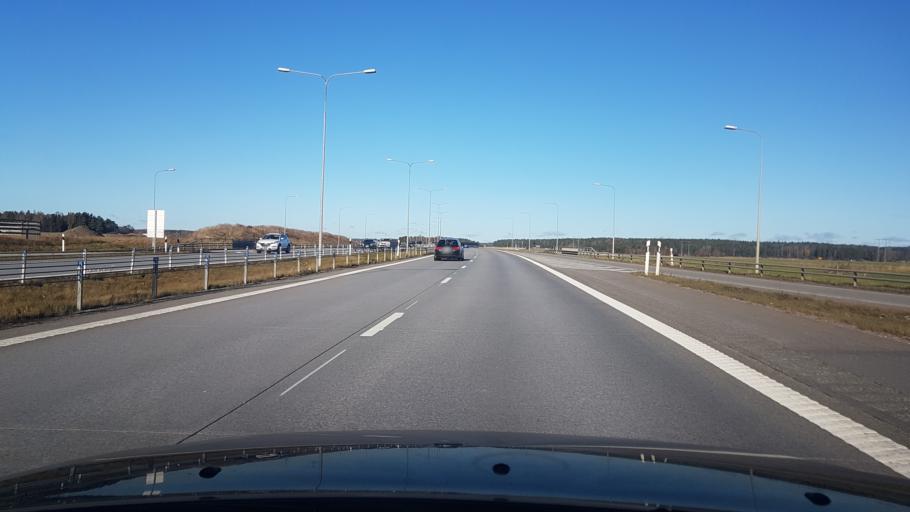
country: SE
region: Uppsala
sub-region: Uppsala Kommun
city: Saevja
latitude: 59.8468
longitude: 17.7343
